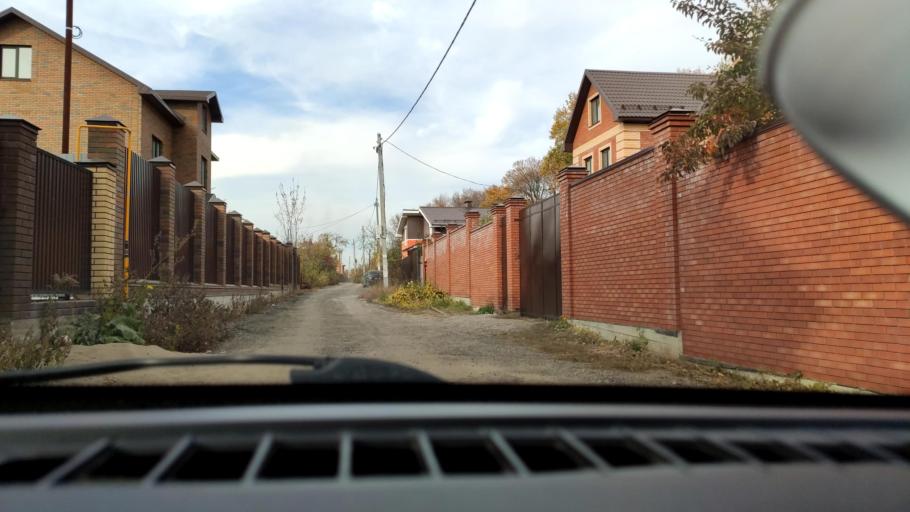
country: RU
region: Samara
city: Petra-Dubrava
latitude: 53.2662
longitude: 50.2646
